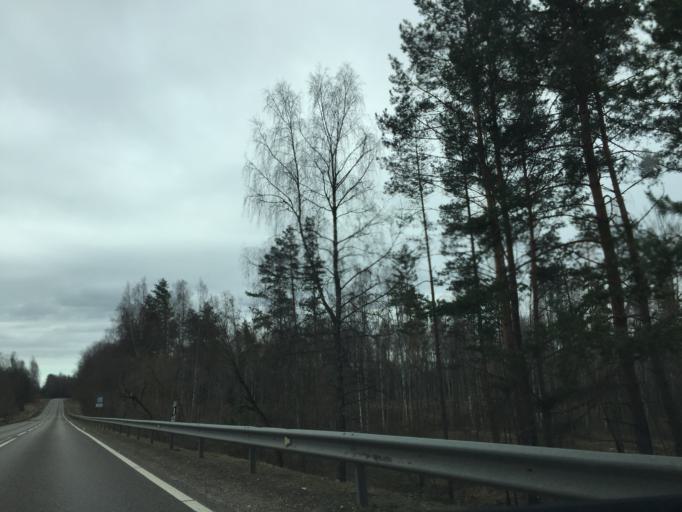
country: LV
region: Kraslavas Rajons
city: Kraslava
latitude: 55.9036
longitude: 27.1108
